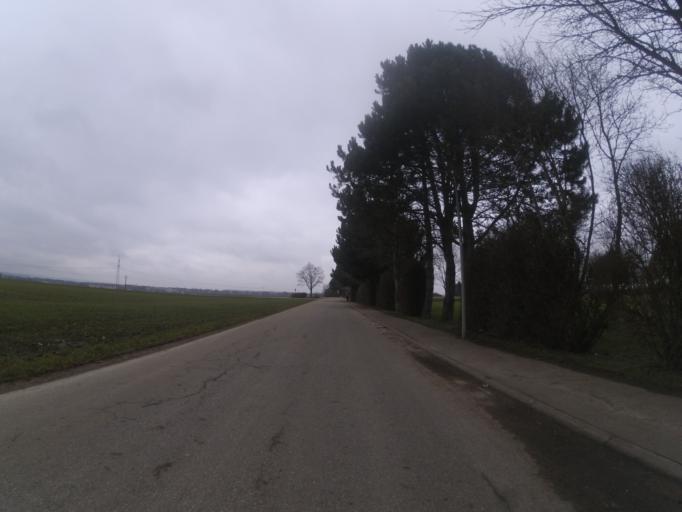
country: DE
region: Baden-Wuerttemberg
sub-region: Tuebingen Region
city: Dornstadt
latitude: 48.4390
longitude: 9.9674
